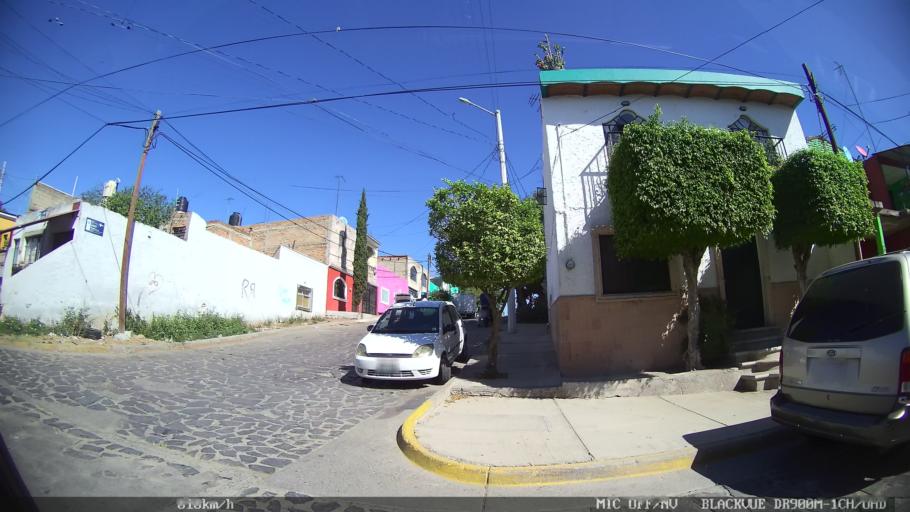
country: MX
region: Jalisco
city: Tlaquepaque
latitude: 20.6802
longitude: -103.2682
